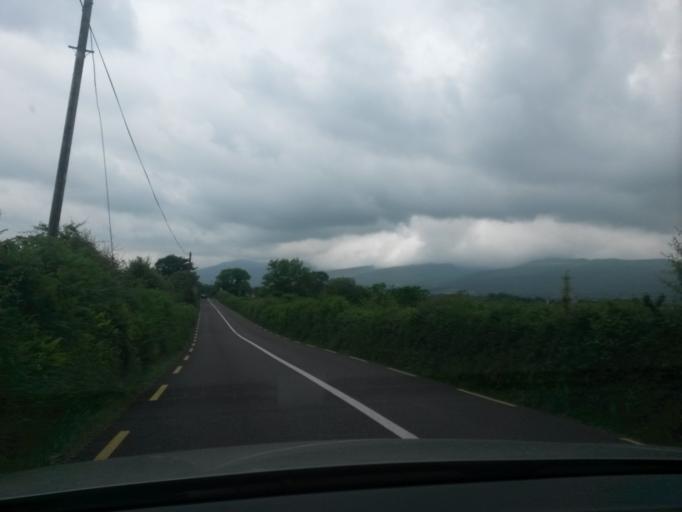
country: IE
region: Munster
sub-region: Ciarrai
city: Tralee
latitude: 52.1633
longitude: -9.6955
